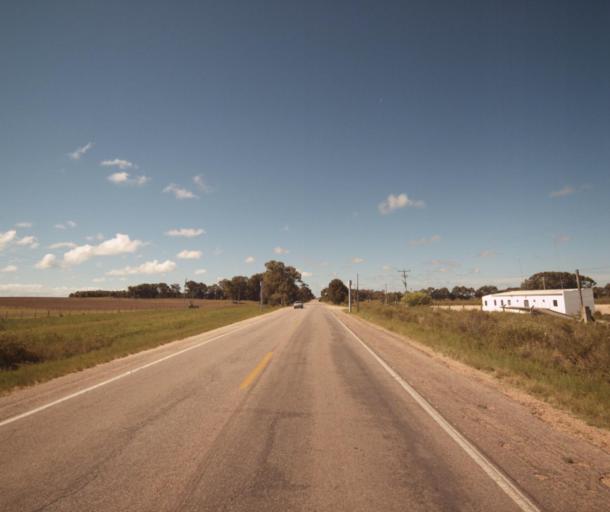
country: BR
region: Rio Grande do Sul
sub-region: Chui
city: Chui
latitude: -33.6646
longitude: -53.4380
